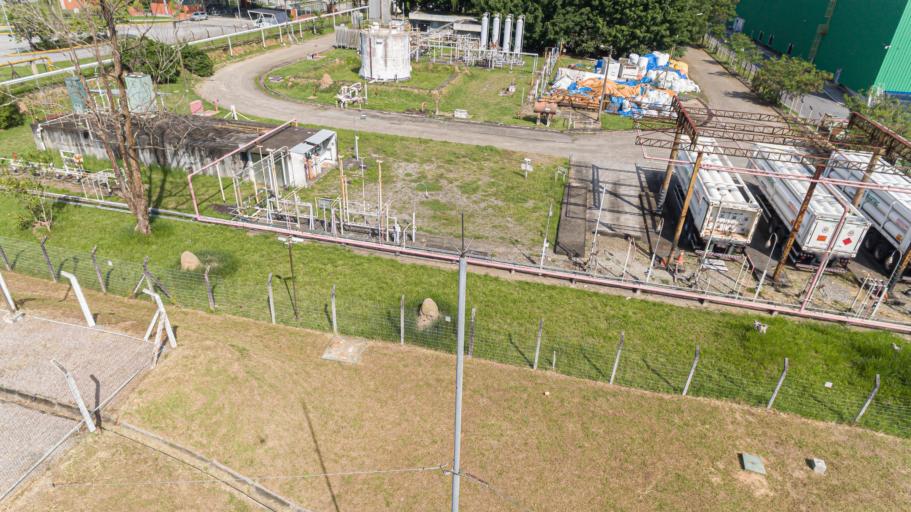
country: BR
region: Sao Paulo
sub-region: Cacapava
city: Cacapava
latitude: -23.1333
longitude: -45.7546
